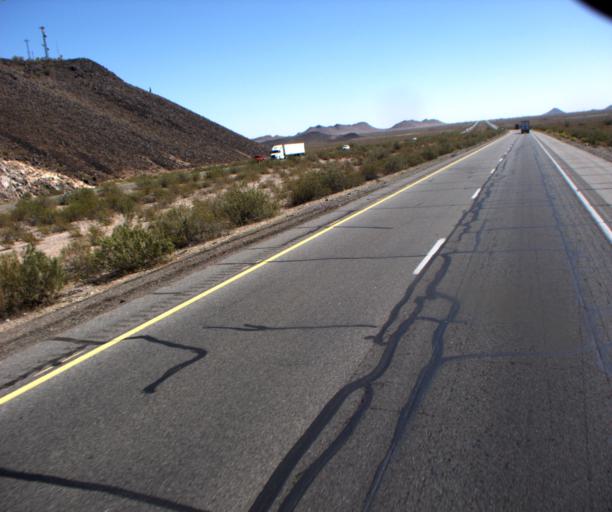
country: US
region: Arizona
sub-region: Maricopa County
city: Buckeye
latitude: 33.5282
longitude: -113.1151
